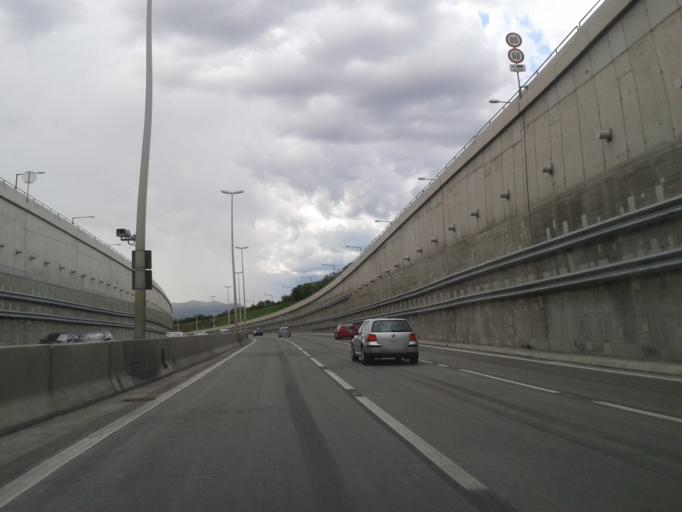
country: AT
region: Lower Austria
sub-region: Politischer Bezirk Wien-Umgebung
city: Leopoldsdorf
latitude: 48.1612
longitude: 16.3847
